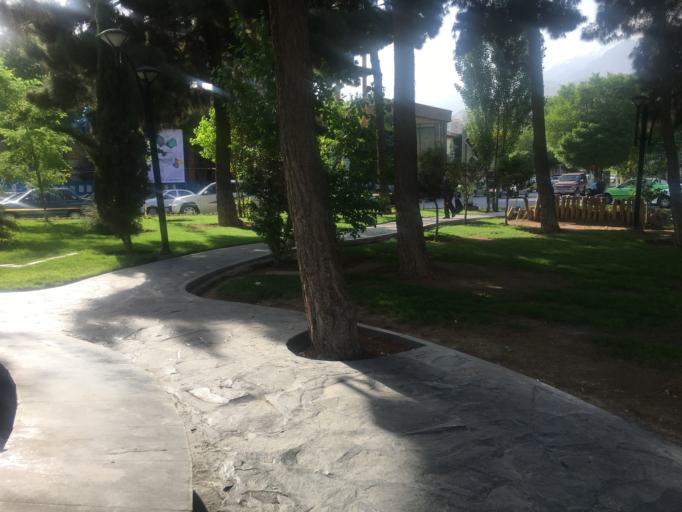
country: IR
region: Tehran
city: Tajrish
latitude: 35.7915
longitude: 51.4778
